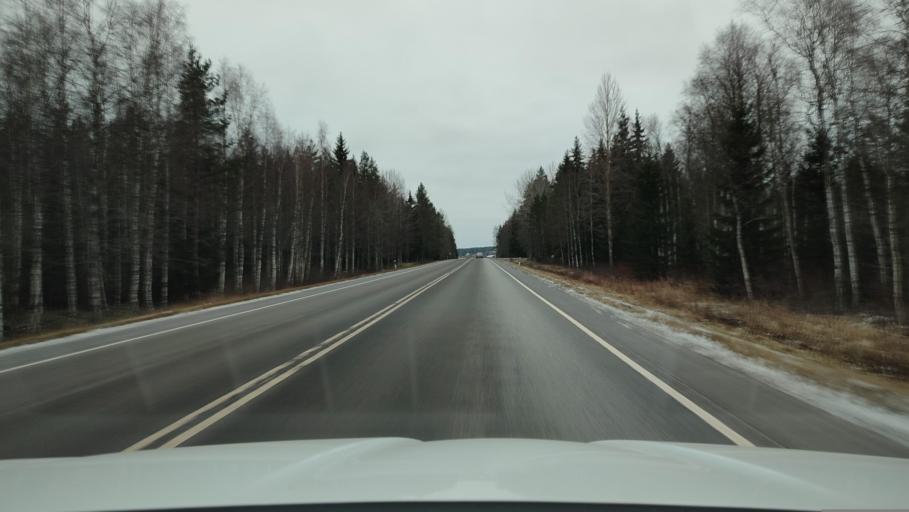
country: FI
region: Ostrobothnia
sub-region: Vaasa
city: Ristinummi
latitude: 62.9376
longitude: 21.7543
